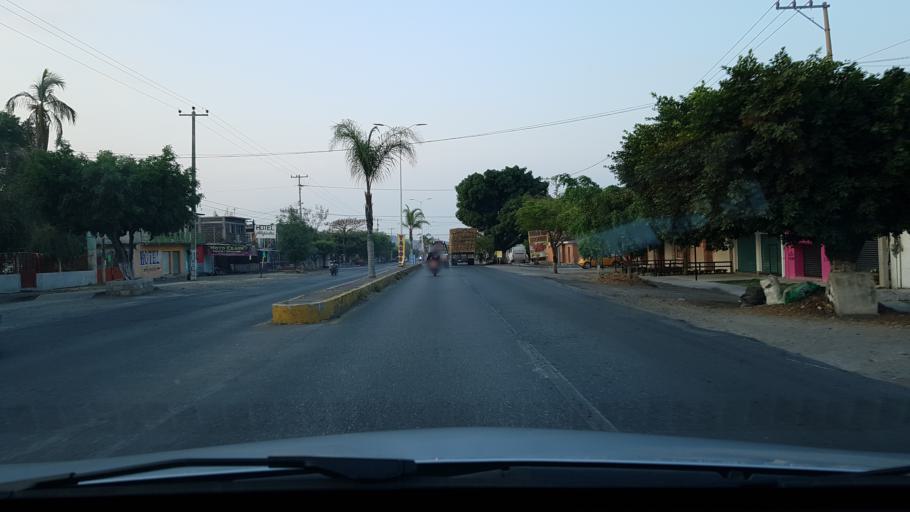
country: MX
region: Morelos
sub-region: Jonacatepec
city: Amacuitlapilco
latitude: 18.6959
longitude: -98.8017
